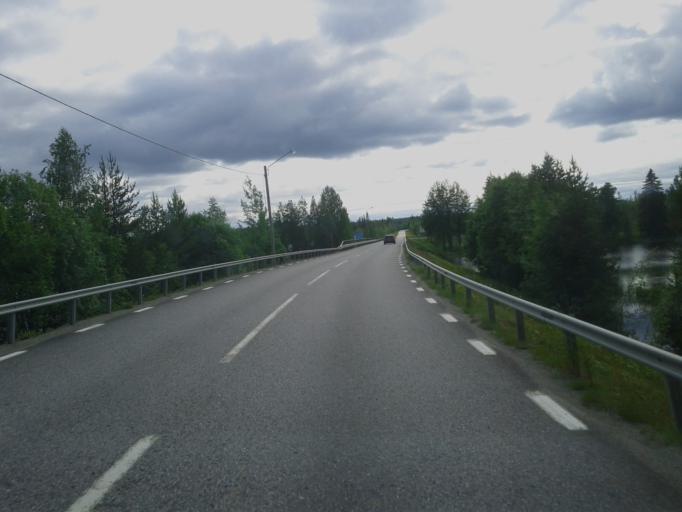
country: SE
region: Vaesterbotten
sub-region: Sorsele Kommun
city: Sorsele
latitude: 65.2096
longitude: 17.6377
